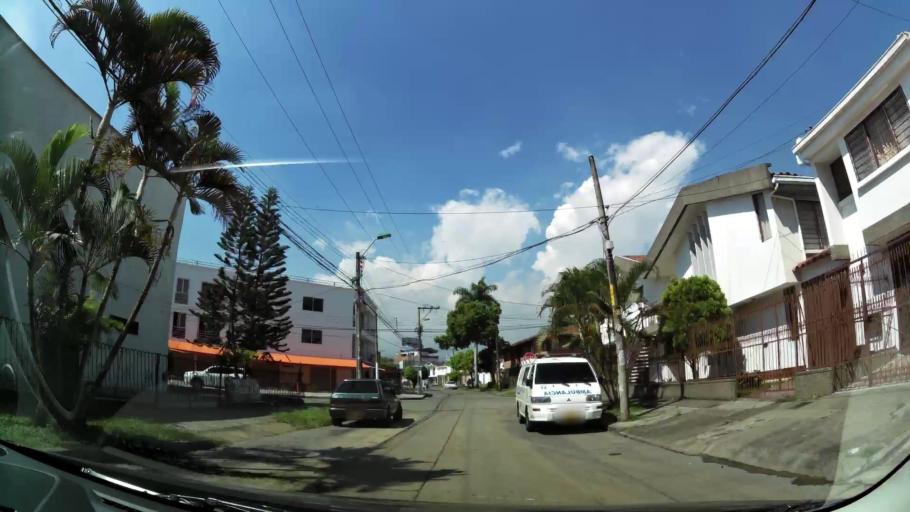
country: CO
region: Valle del Cauca
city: Cali
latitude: 3.4280
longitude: -76.5315
